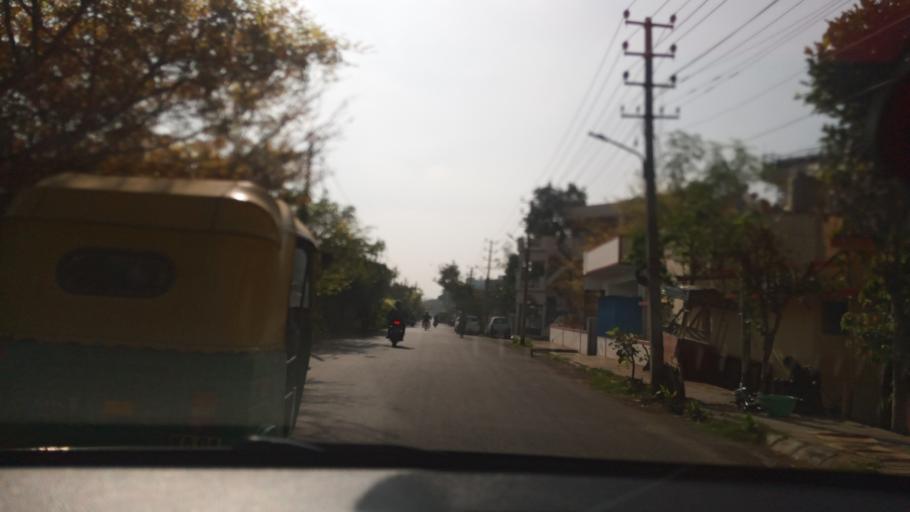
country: IN
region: Karnataka
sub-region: Bangalore Urban
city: Yelahanka
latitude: 13.0476
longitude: 77.5502
